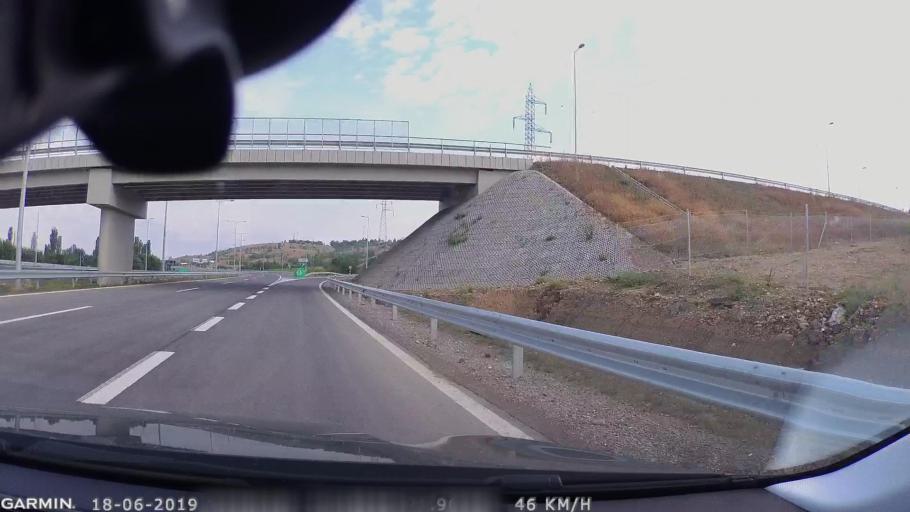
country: MK
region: Sveti Nikole
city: Sveti Nikole
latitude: 41.8555
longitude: 21.9629
